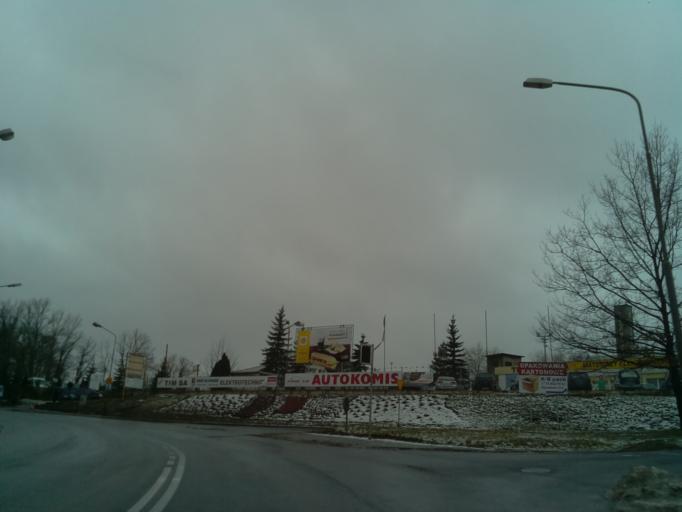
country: PL
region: Lower Silesian Voivodeship
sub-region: Powiat walbrzyski
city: Szczawno-Zdroj
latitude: 50.8123
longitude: 16.2967
